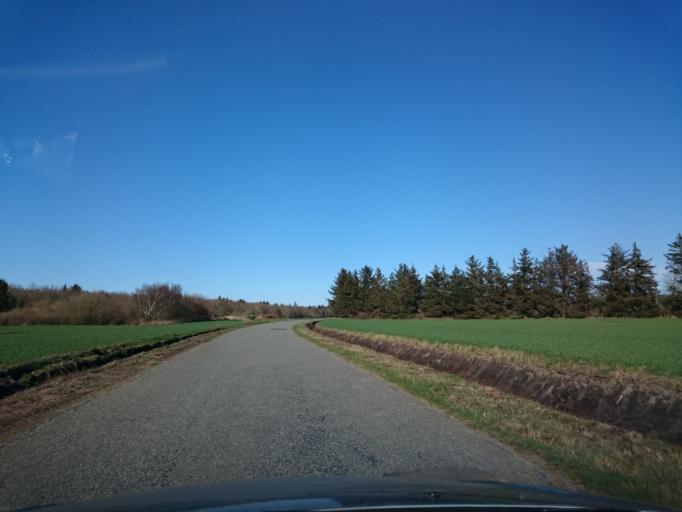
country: DK
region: North Denmark
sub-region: Hjorring Kommune
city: Hirtshals
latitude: 57.5601
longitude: 10.0721
